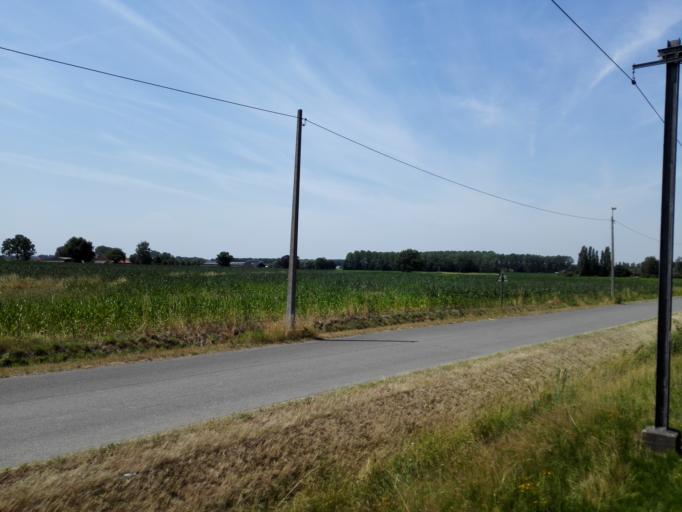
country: BE
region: Flanders
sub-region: Provincie Antwerpen
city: Berlaar
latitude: 51.1203
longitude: 4.6267
